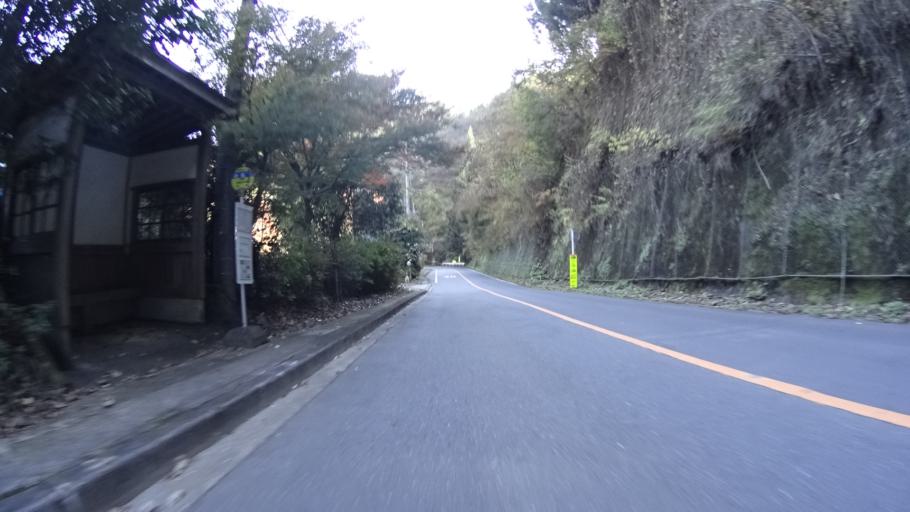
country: JP
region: Yamanashi
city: Uenohara
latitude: 35.7201
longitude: 139.0657
